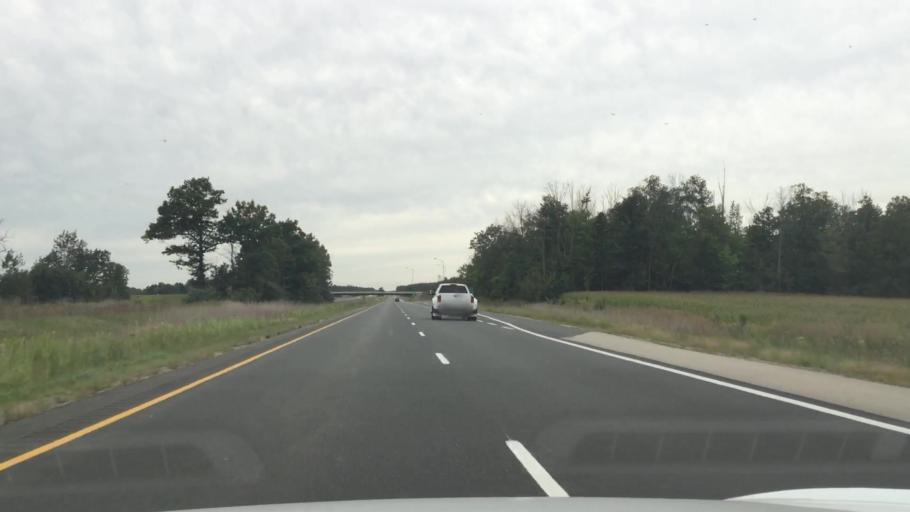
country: CA
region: Ontario
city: Lambton Shores
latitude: 42.9923
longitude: -81.8705
